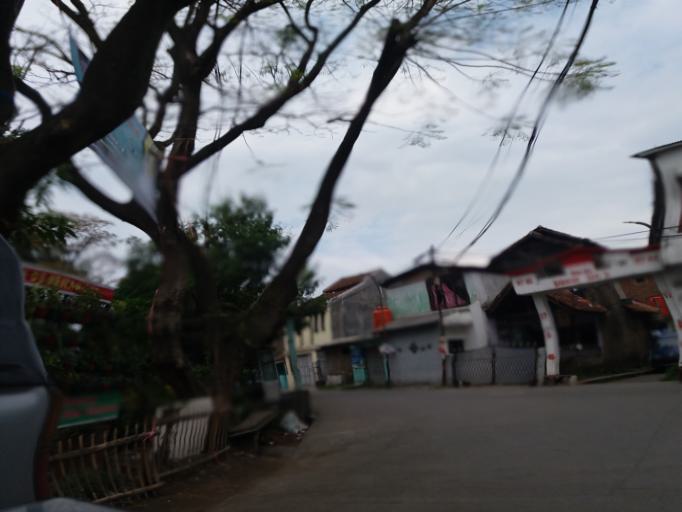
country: ID
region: West Java
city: Bandung
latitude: -6.9246
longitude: 107.6491
